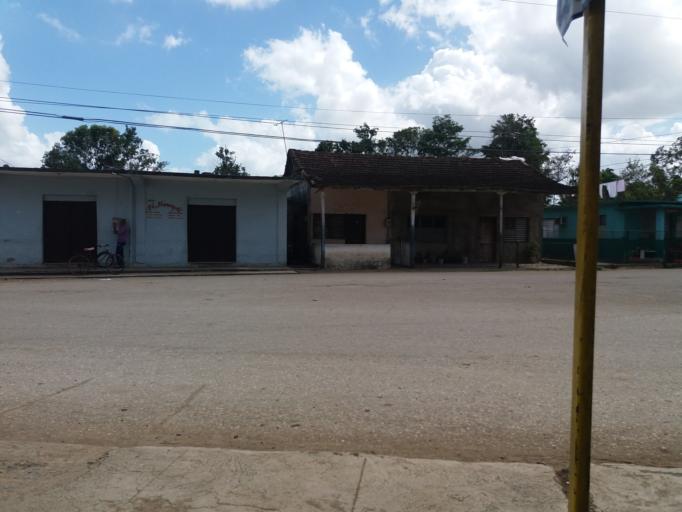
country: CU
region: Cienfuegos
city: Rodas
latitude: 22.4261
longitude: -80.4587
